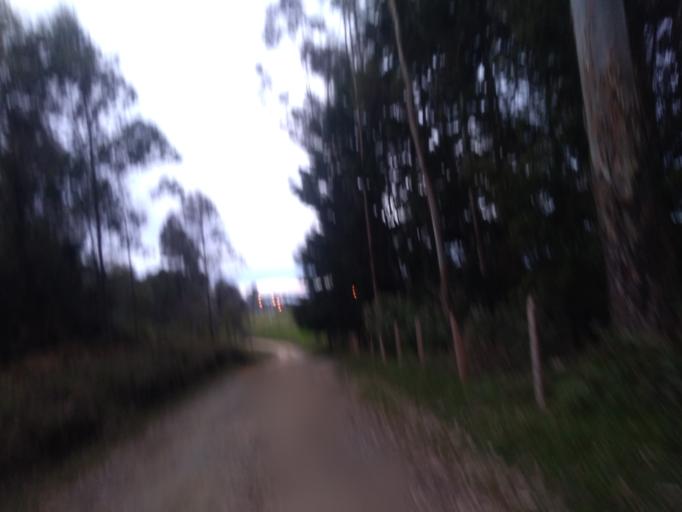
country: CO
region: Antioquia
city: Bello
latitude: 6.3550
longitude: -75.6084
